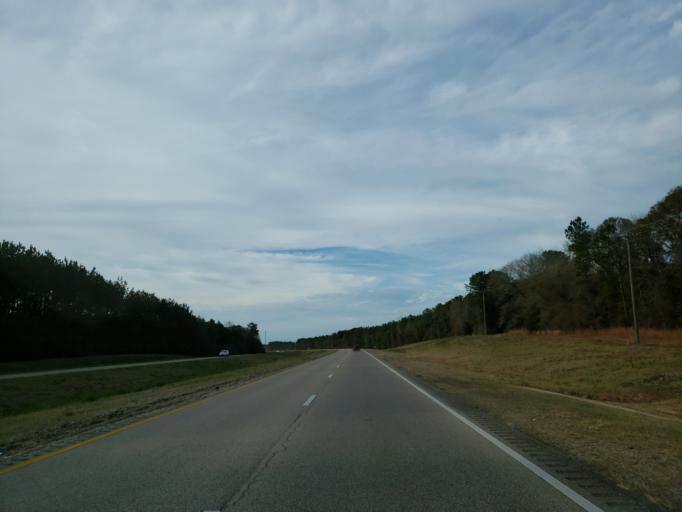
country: US
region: Mississippi
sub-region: Wayne County
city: Belmont
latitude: 31.5989
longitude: -88.5555
